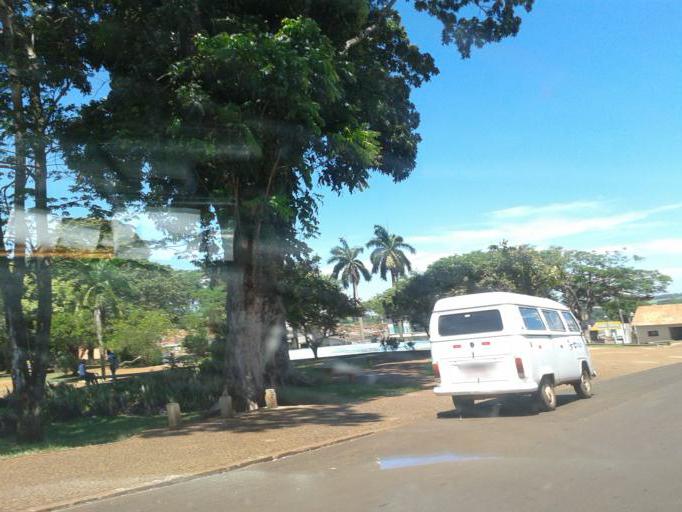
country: BR
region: Minas Gerais
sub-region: Capinopolis
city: Capinopolis
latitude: -18.6841
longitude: -49.5683
